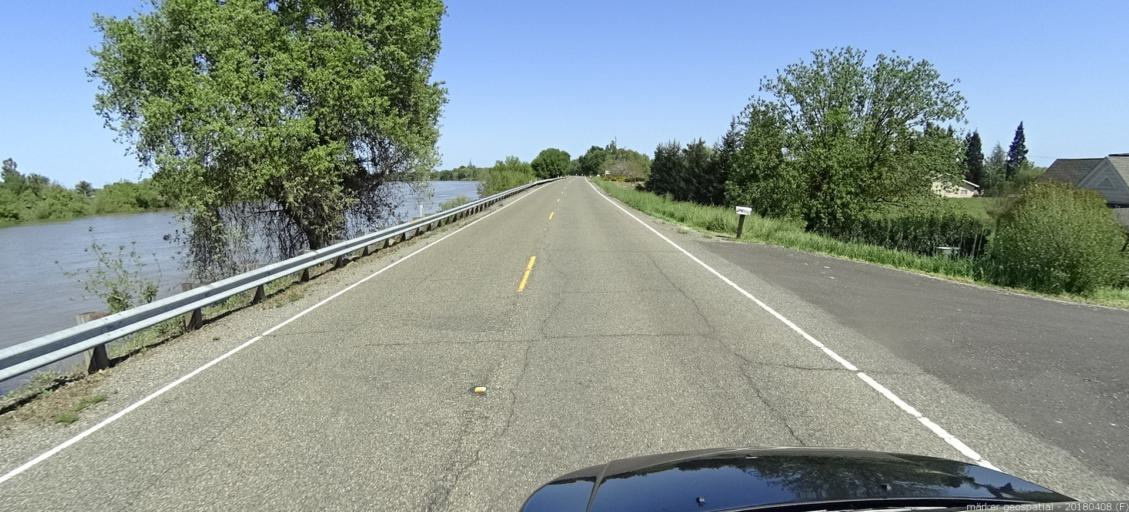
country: US
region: California
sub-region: Sacramento County
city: Parkway
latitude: 38.4340
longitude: -121.5198
